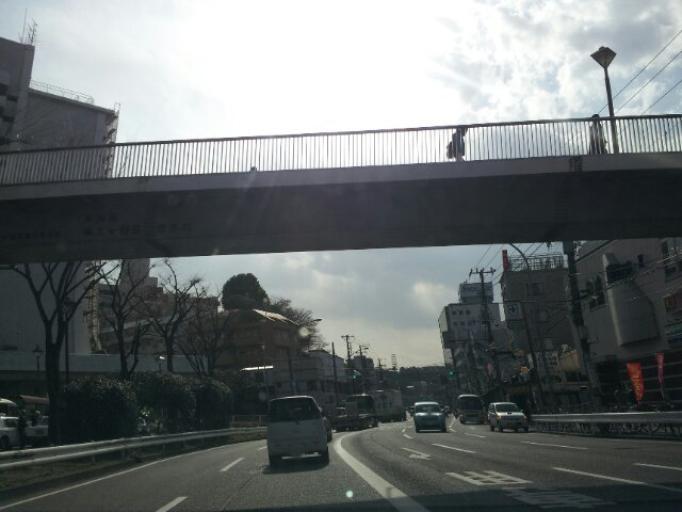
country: JP
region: Kanagawa
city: Yokohama
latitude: 35.4465
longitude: 139.6001
